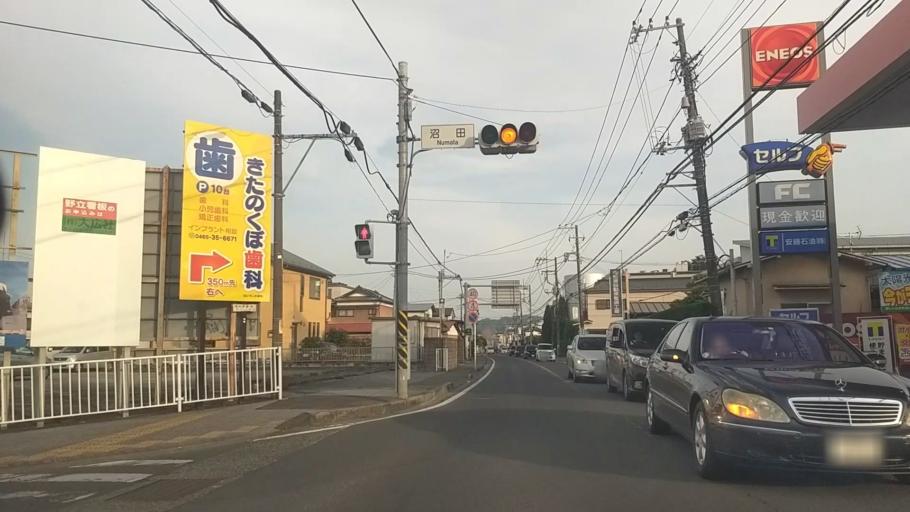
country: JP
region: Kanagawa
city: Odawara
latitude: 35.2939
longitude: 139.1321
